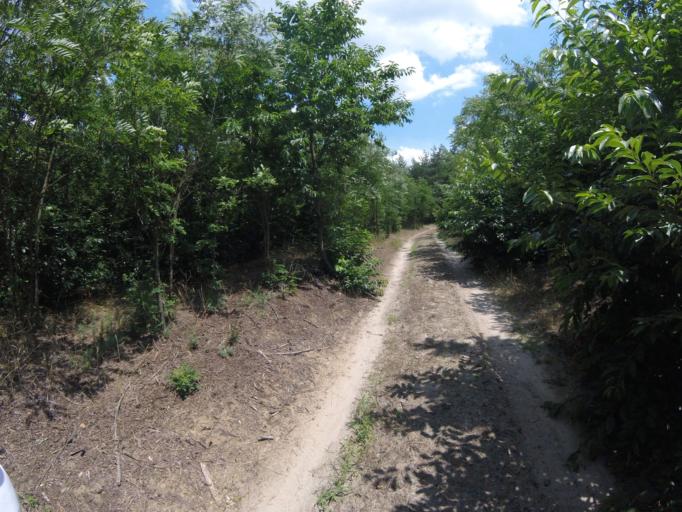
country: HU
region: Pest
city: Nagykoros
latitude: 47.0684
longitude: 19.7360
